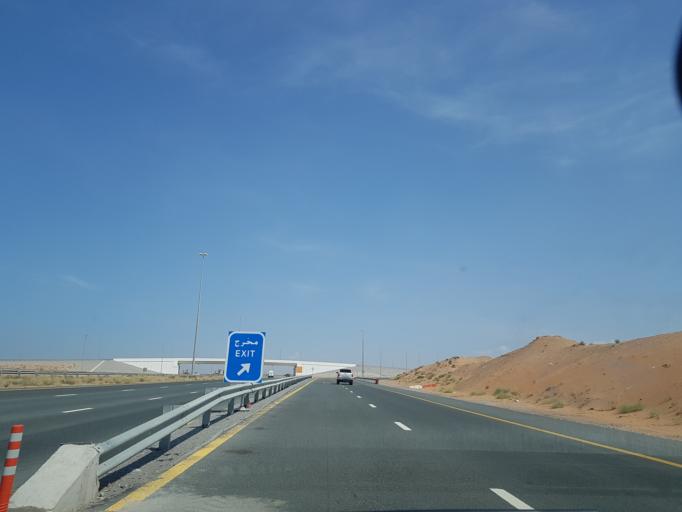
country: AE
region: Ra's al Khaymah
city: Ras al-Khaimah
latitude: 25.6692
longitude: 55.8790
